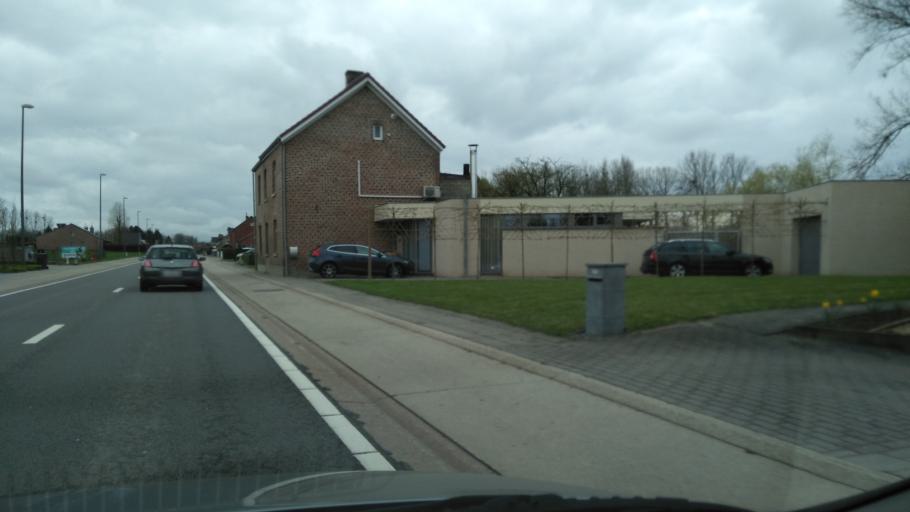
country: BE
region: Flanders
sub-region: Provincie Limburg
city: Bilzen
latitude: 50.8506
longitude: 5.5386
